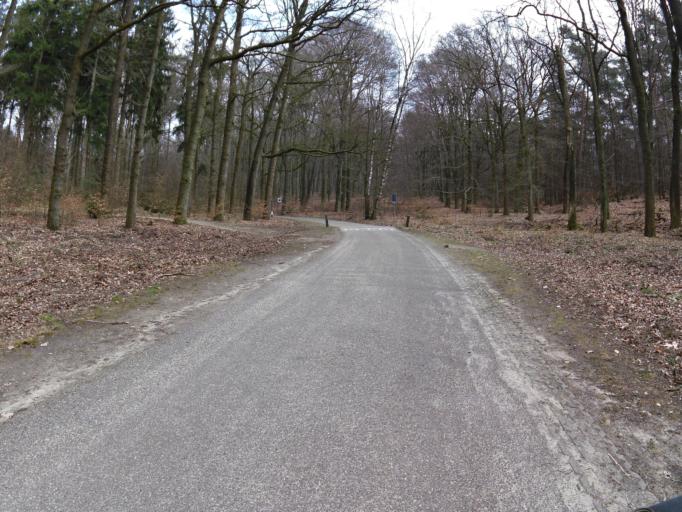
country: NL
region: Gelderland
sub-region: Gemeente Rozendaal
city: Rozendaal
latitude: 52.0111
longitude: 5.9693
